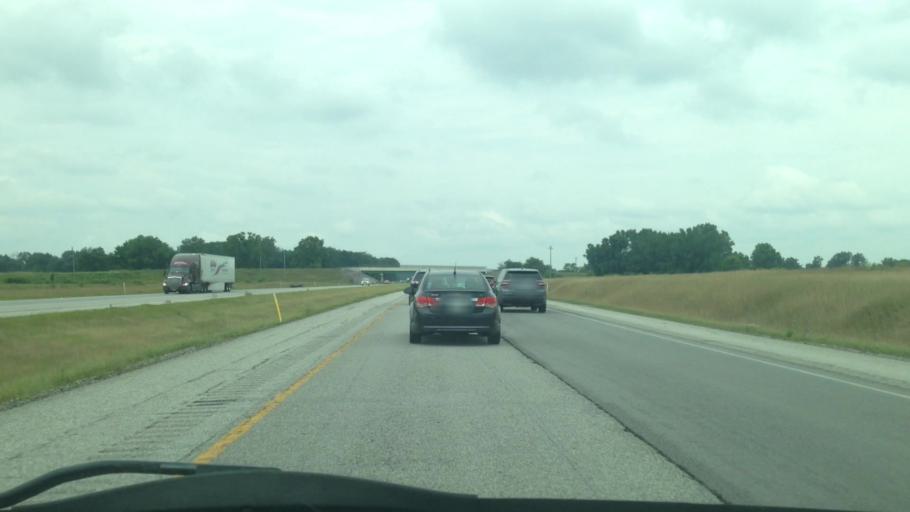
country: US
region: Michigan
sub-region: Saint Joseph County
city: White Pigeon
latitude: 41.7495
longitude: -85.5589
